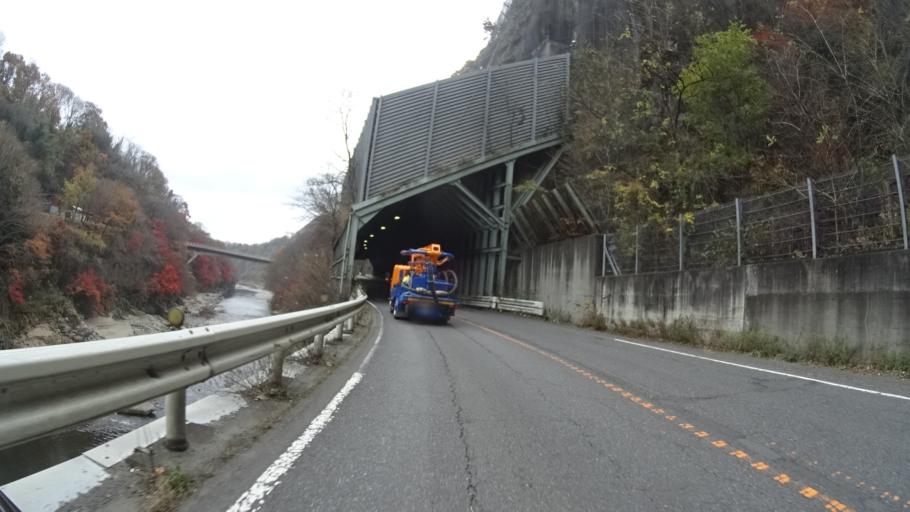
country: JP
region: Gunma
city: Numata
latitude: 36.5836
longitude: 139.0498
